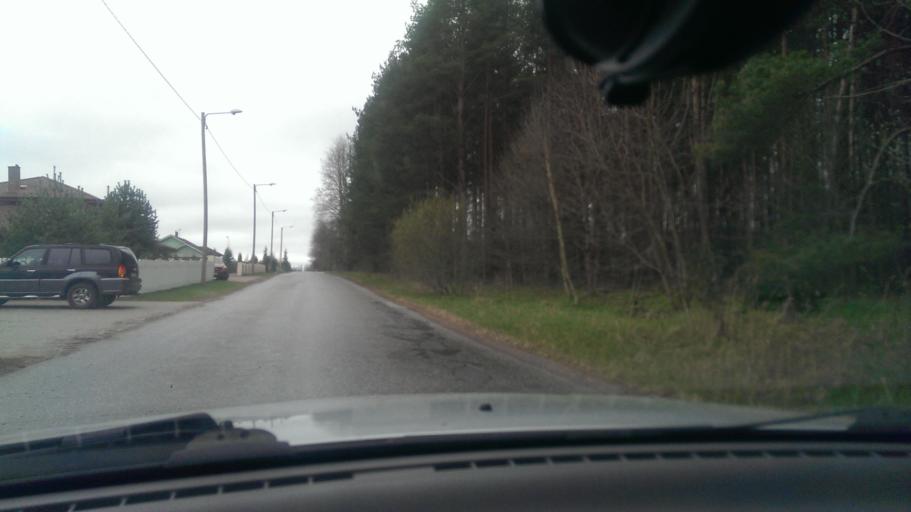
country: EE
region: Tartu
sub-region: Tartu linn
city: Tartu
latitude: 58.3566
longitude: 26.7943
